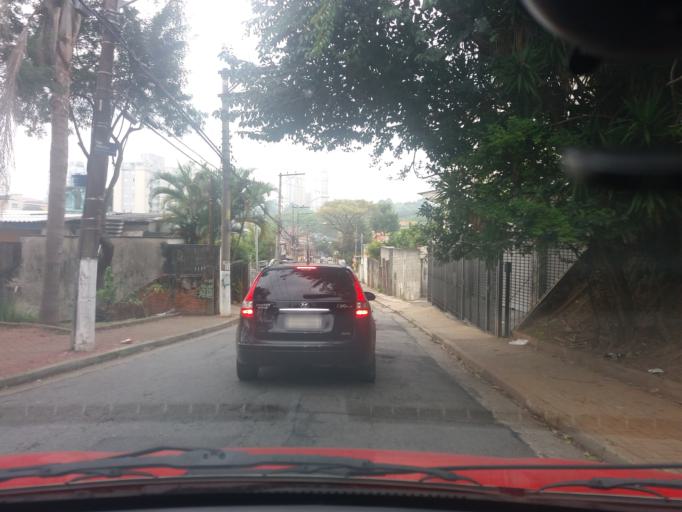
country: BR
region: Sao Paulo
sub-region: Taboao Da Serra
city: Taboao da Serra
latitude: -23.6012
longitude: -46.7346
